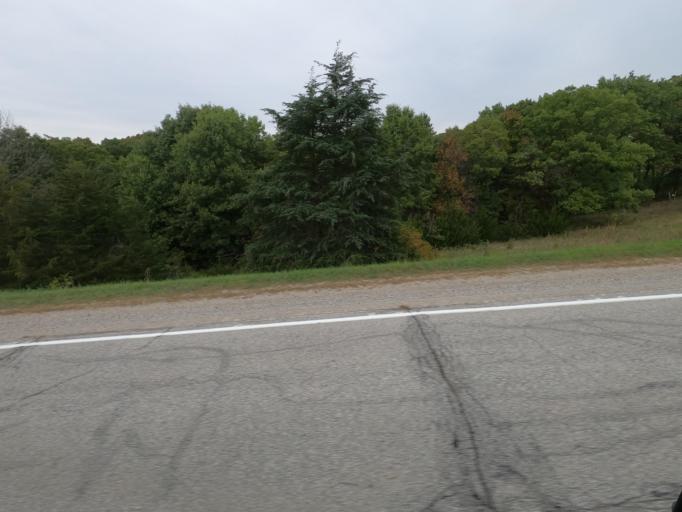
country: US
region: Iowa
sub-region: Van Buren County
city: Keosauqua
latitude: 40.8350
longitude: -91.9673
